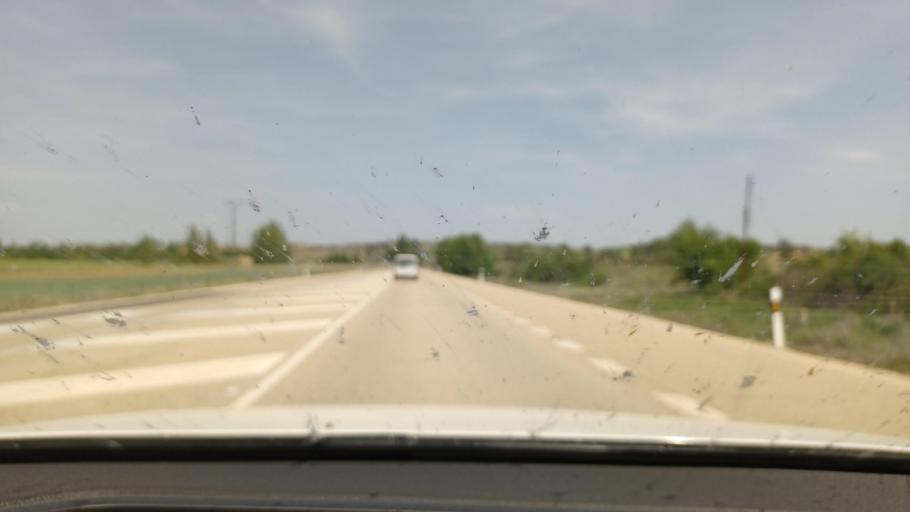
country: ES
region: Castille and Leon
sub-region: Provincia de Soria
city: Barca
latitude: 41.4653
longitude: -2.6179
